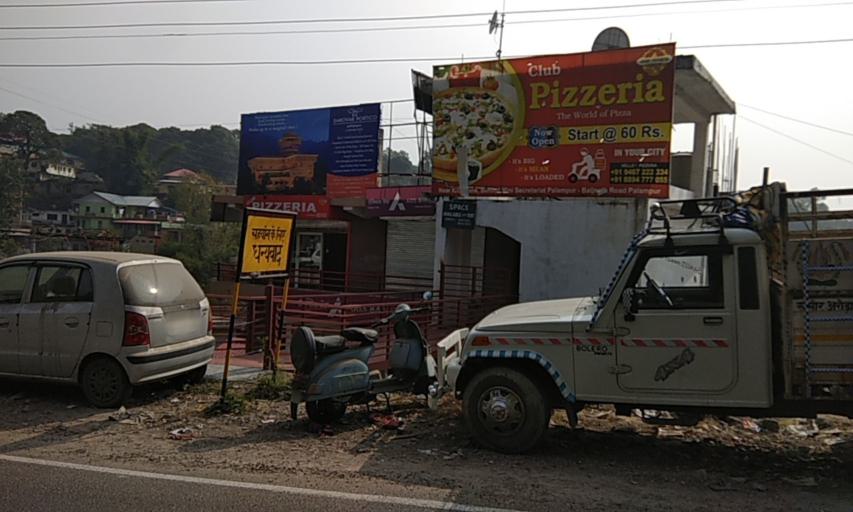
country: IN
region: Himachal Pradesh
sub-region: Kangra
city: Palampur
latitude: 32.1092
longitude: 76.5375
